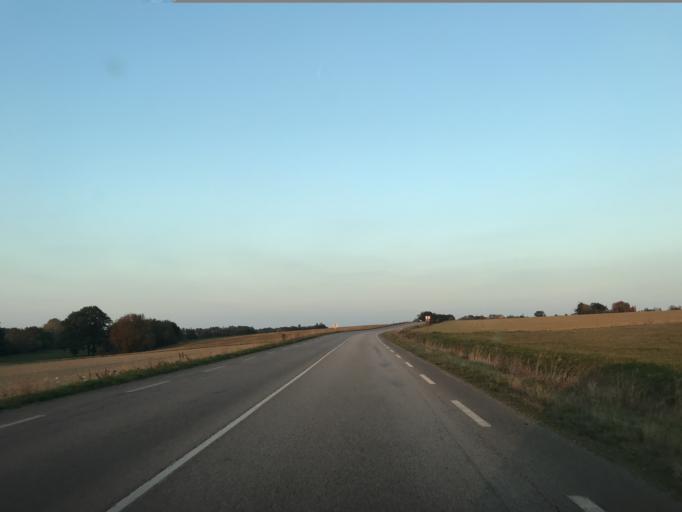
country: FR
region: Haute-Normandie
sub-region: Departement de l'Eure
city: Bourth
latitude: 48.6884
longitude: 0.8137
